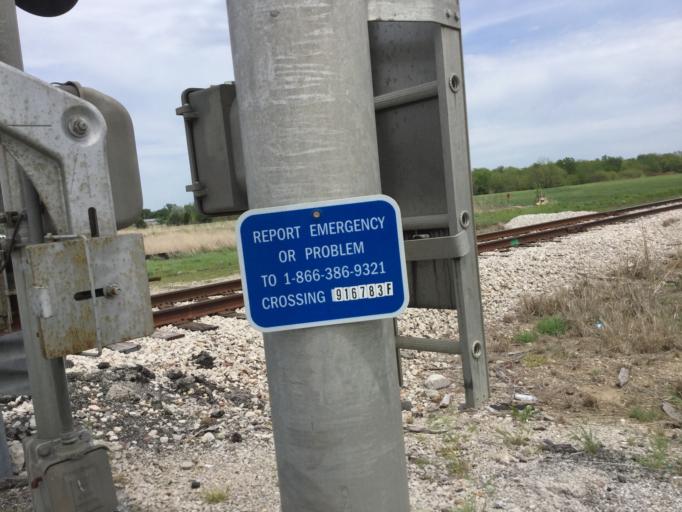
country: US
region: Kansas
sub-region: Montgomery County
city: Cherryvale
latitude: 37.2628
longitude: -95.5680
